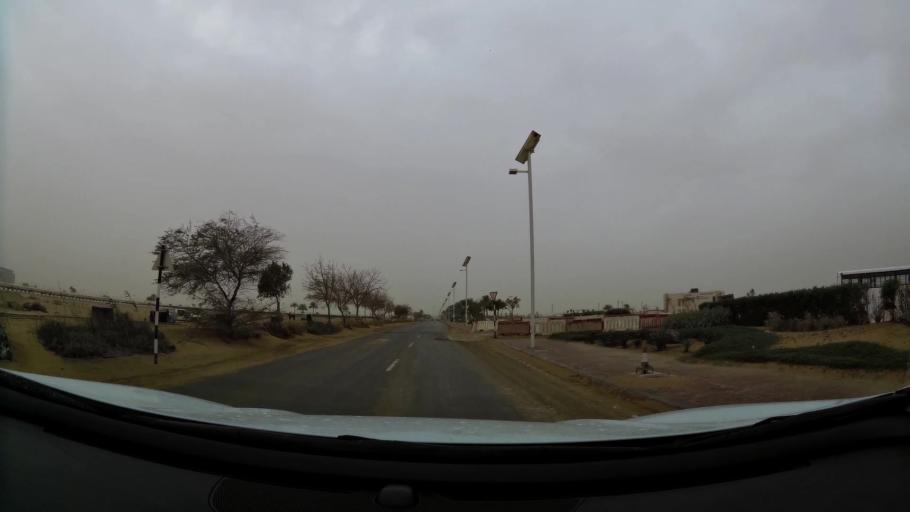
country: AE
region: Abu Dhabi
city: Abu Dhabi
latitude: 24.4362
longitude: 54.6145
